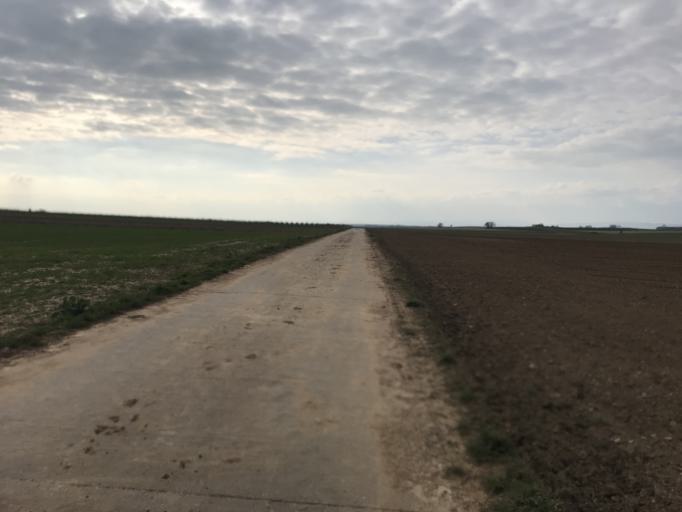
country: DE
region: Rheinland-Pfalz
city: Essenheim
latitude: 49.9453
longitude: 8.1683
